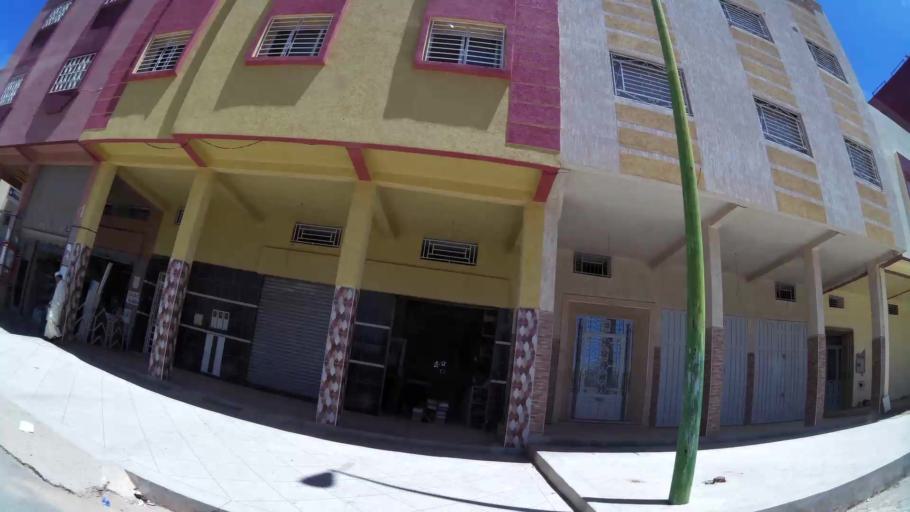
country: MA
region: Meknes-Tafilalet
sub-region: Meknes
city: Meknes
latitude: 33.8561
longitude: -5.5526
